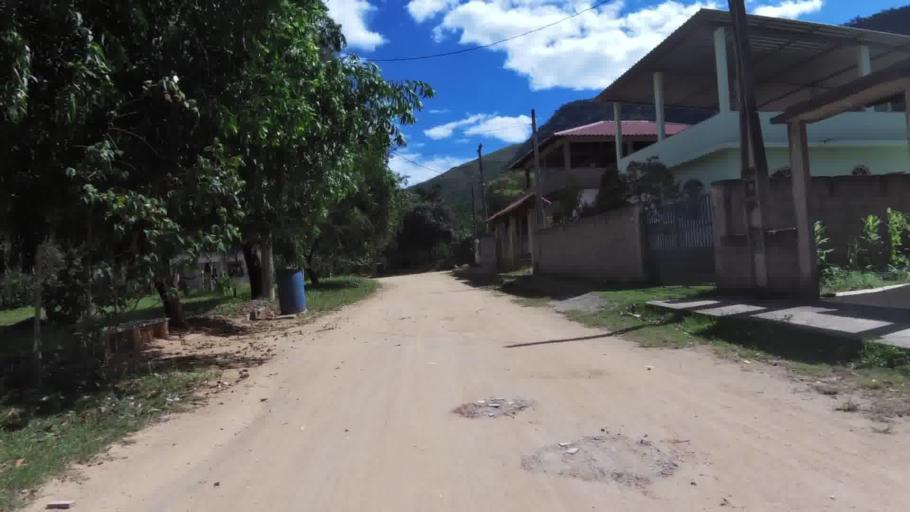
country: BR
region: Espirito Santo
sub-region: Rio Novo Do Sul
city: Rio Novo do Sul
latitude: -20.8620
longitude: -40.9495
